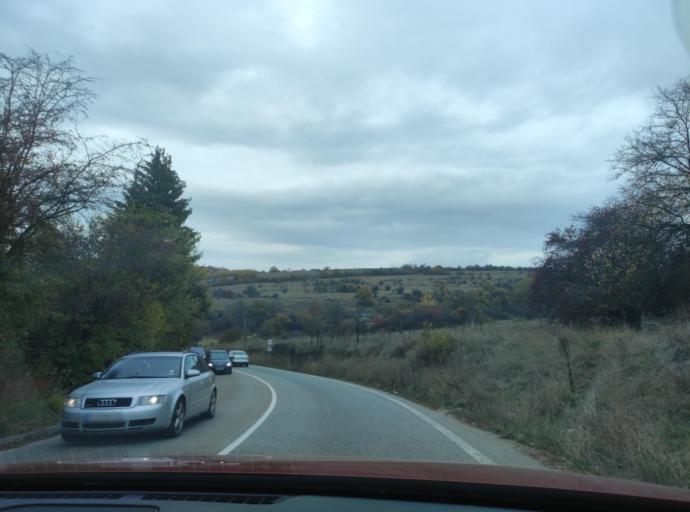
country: BG
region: Sofiya
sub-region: Obshtina Godech
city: Godech
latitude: 42.9638
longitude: 23.1562
